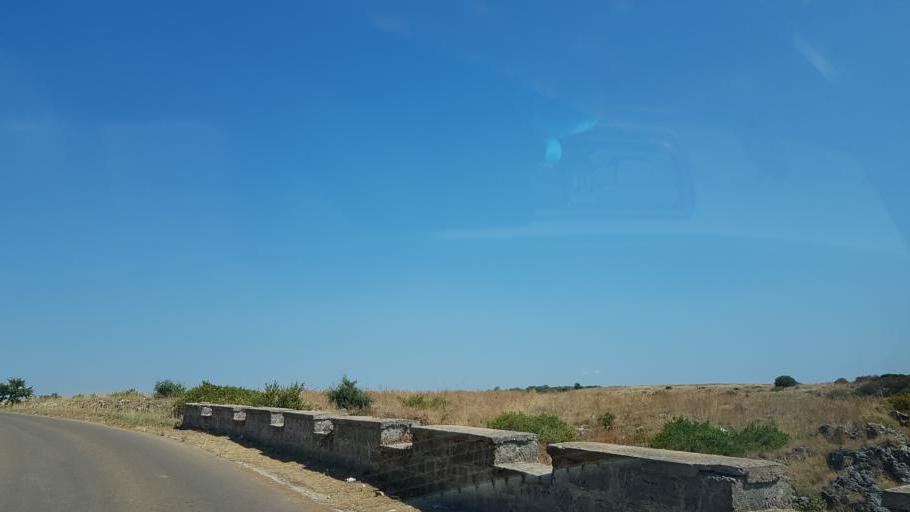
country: IT
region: Apulia
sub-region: Provincia di Lecce
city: Nardo
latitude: 40.1744
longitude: 17.9481
